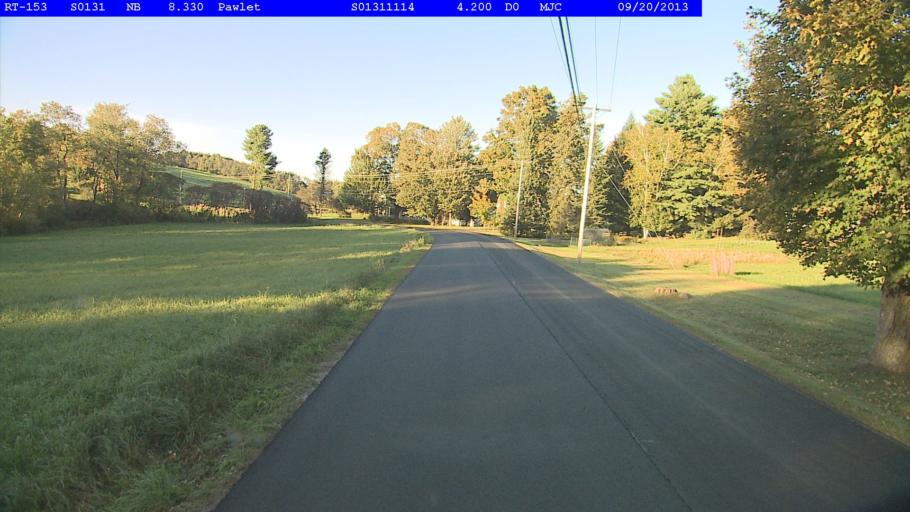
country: US
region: New York
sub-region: Washington County
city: Granville
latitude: 43.3671
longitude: -73.2350
